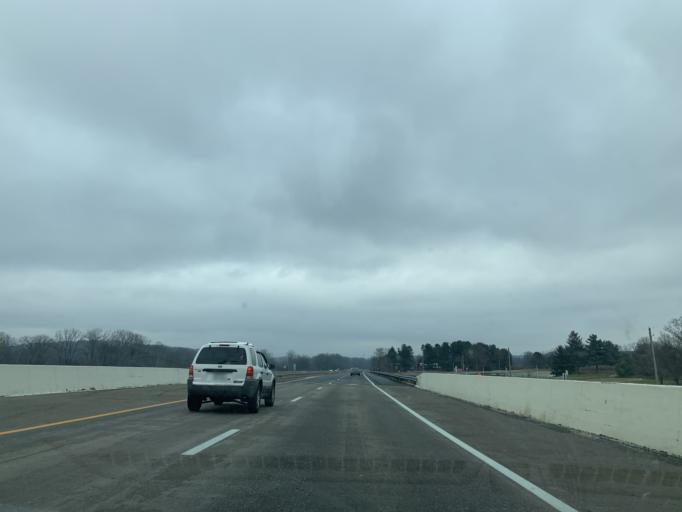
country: US
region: Ohio
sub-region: Licking County
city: Granville South
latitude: 40.0698
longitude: -82.5611
